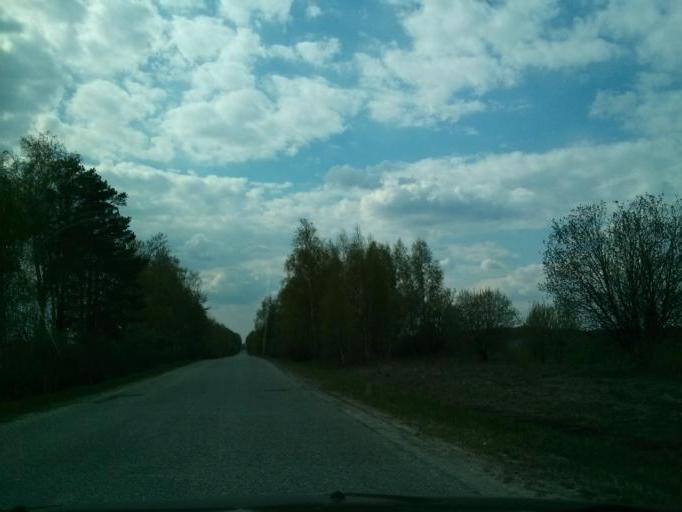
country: RU
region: Nizjnij Novgorod
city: Shimorskoye
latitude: 55.3381
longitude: 41.8881
